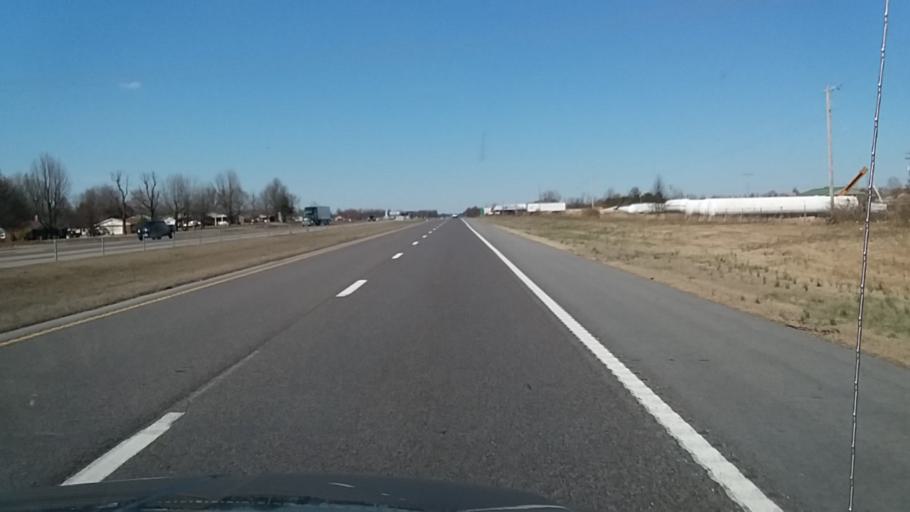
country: US
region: Missouri
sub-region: Scott County
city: Sikeston
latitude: 36.9573
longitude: -89.5341
